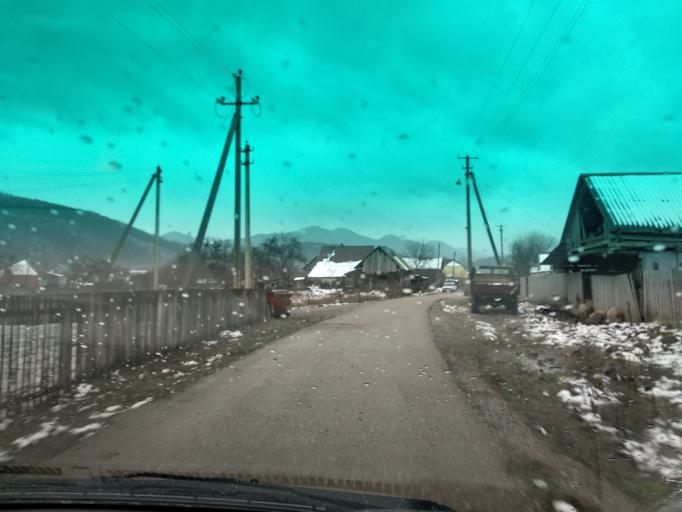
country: RU
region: Krasnodarskiy
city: Khadyzhensk
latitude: 44.2114
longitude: 39.4238
